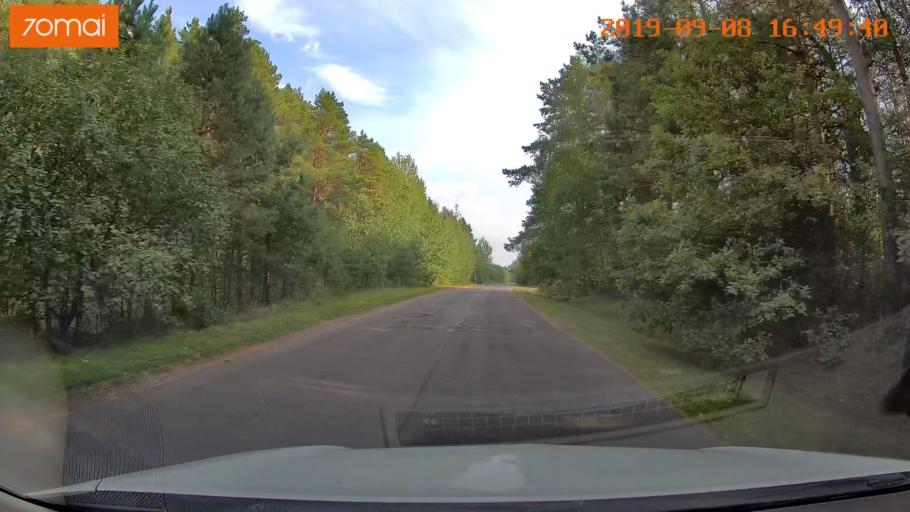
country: BY
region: Grodnenskaya
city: Hrodna
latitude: 53.8082
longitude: 23.8778
